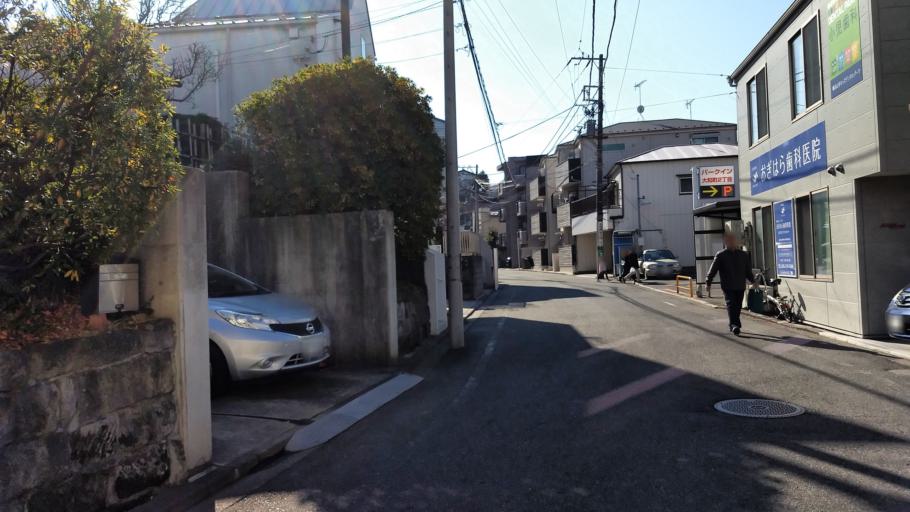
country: JP
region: Kanagawa
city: Yokohama
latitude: 35.4294
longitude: 139.6474
